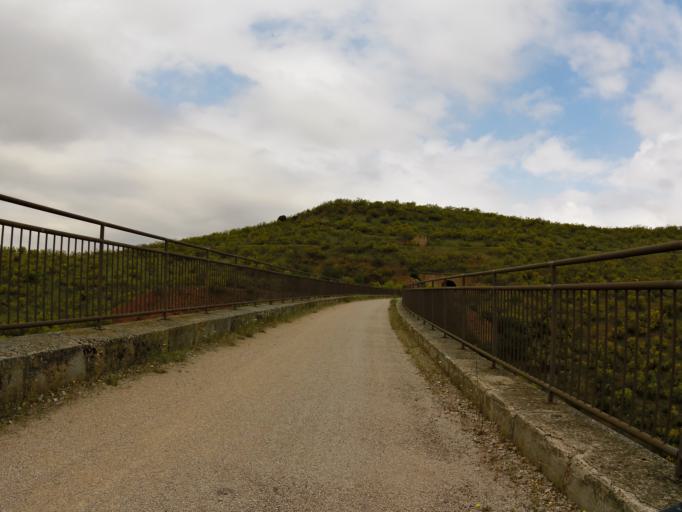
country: ES
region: Castille-La Mancha
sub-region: Provincia de Albacete
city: Alcaraz
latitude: 38.7008
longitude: -2.4970
